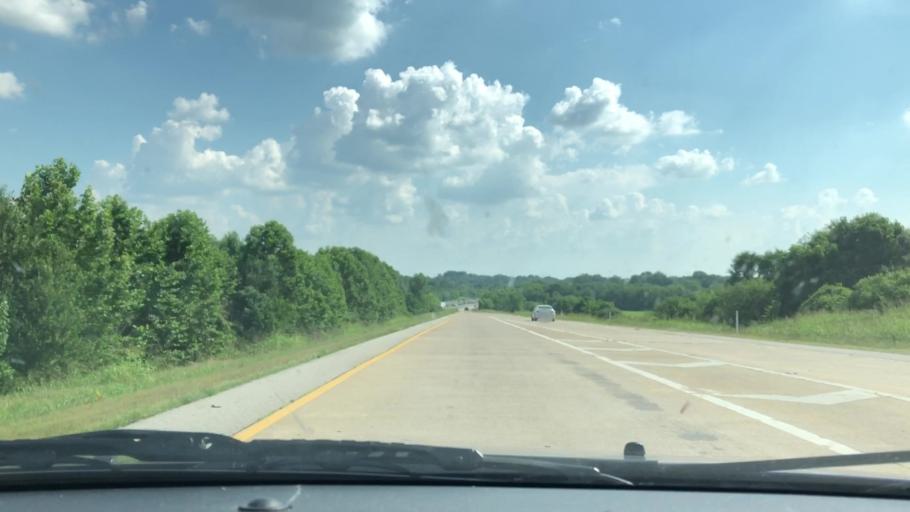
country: US
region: Tennessee
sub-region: Williamson County
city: Thompson's Station
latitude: 35.8165
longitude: -86.8439
